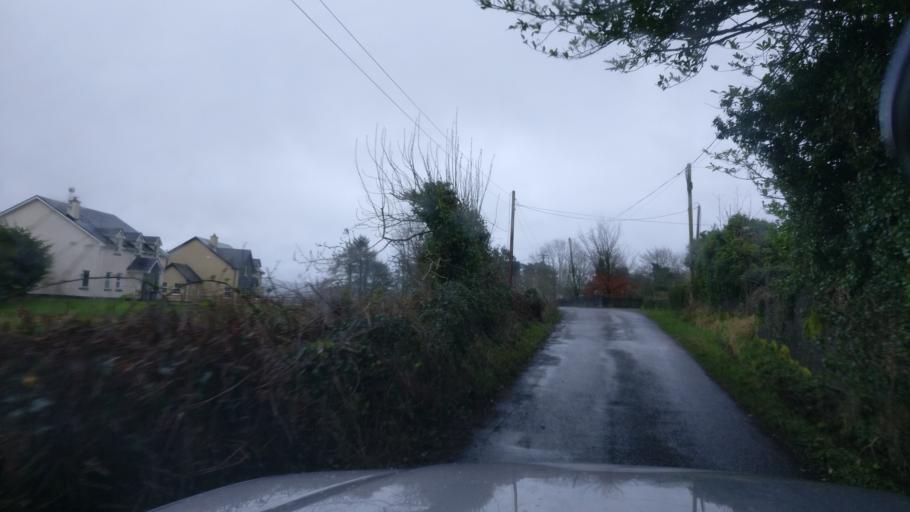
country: IE
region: Connaught
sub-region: County Galway
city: Loughrea
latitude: 53.1690
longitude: -8.6451
